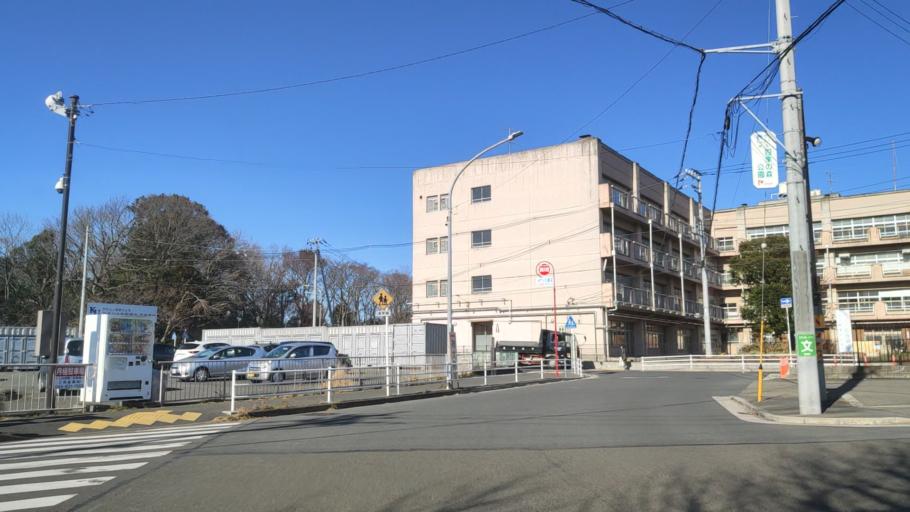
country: JP
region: Kanagawa
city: Minami-rinkan
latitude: 35.5028
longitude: 139.5302
